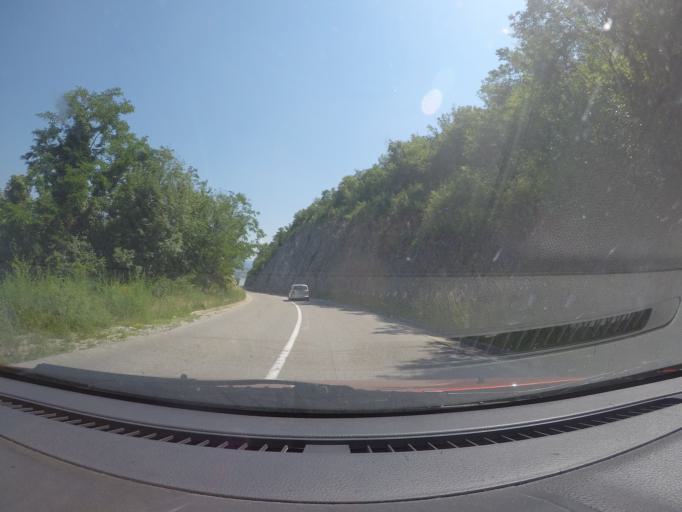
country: RO
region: Mehedinti
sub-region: Comuna Eselnita
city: Eselnita
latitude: 44.6636
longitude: 22.3371
